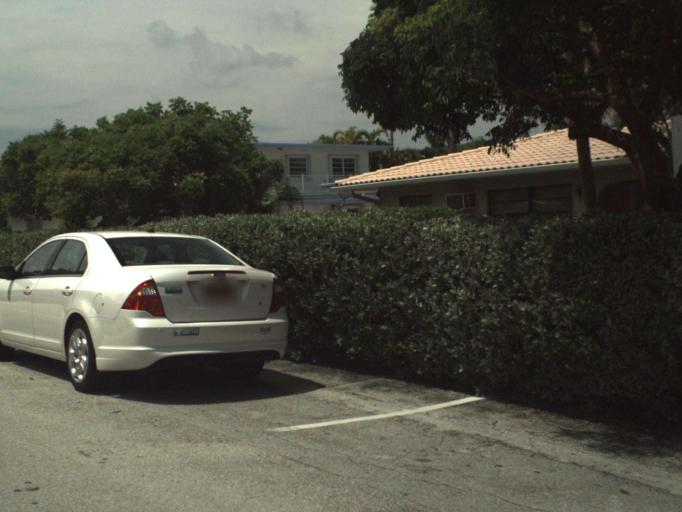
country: US
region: Florida
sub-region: Broward County
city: Hillsboro Beach
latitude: 26.3072
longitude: -80.0777
